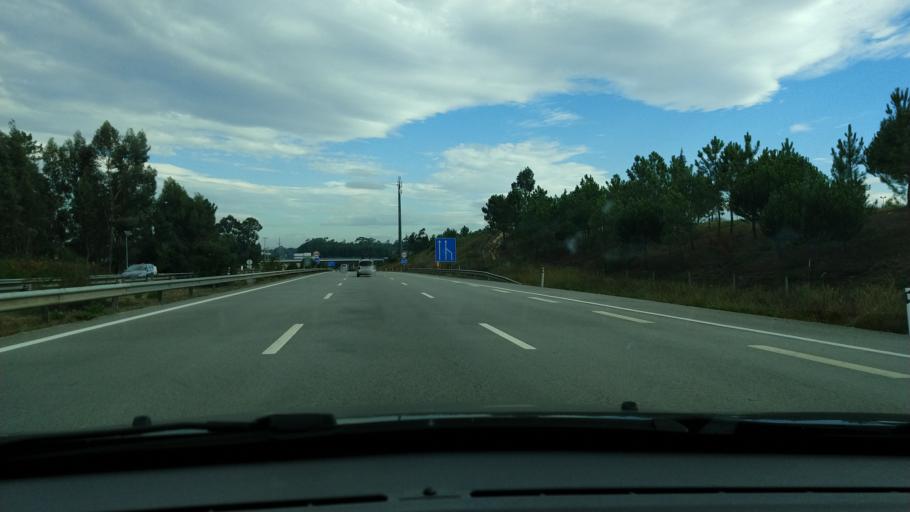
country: PT
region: Aveiro
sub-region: Aveiro
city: Eixo
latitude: 40.6493
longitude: -8.5956
